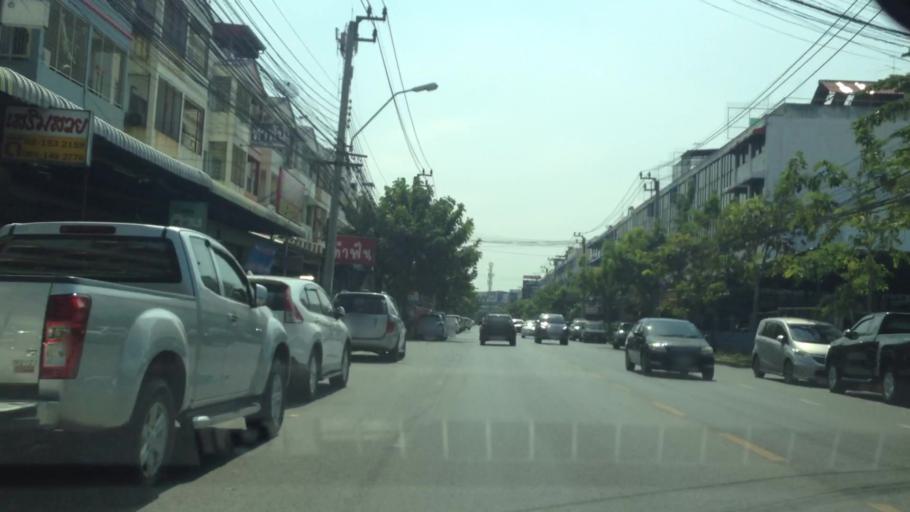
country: TH
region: Bangkok
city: Sai Mai
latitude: 13.8989
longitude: 100.6380
